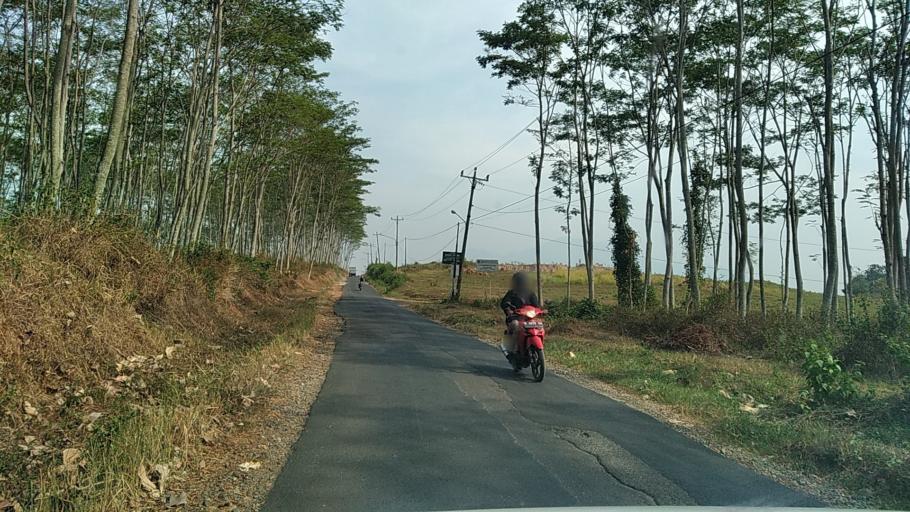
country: ID
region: Central Java
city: Semarang
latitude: -7.0346
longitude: 110.3152
